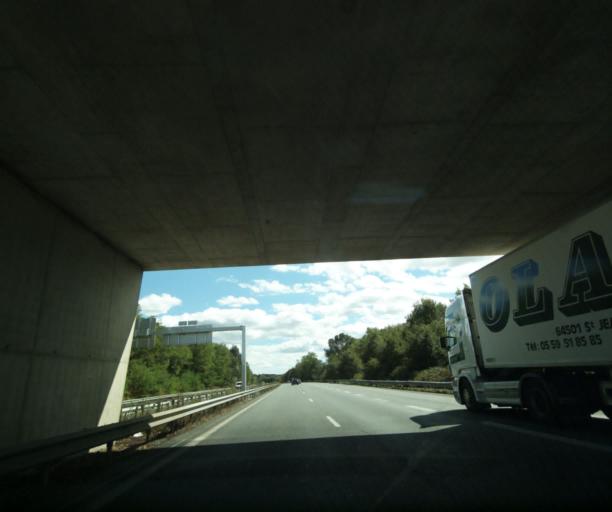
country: FR
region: Aquitaine
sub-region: Departement de la Gironde
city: Toulenne
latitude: 44.5408
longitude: -0.2631
